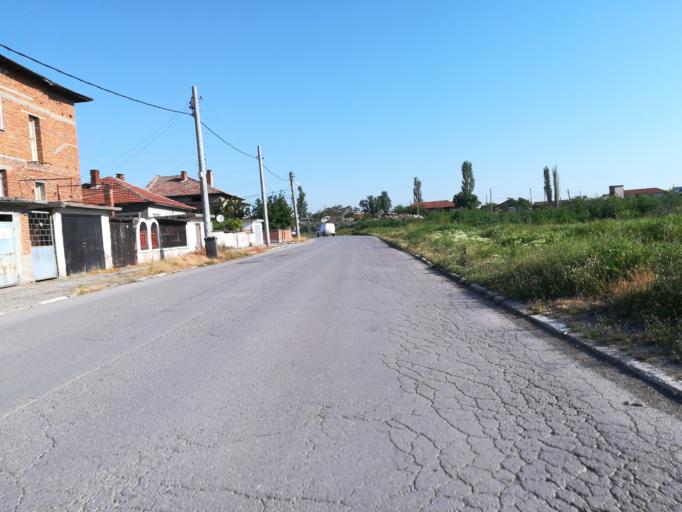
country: BG
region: Stara Zagora
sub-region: Obshtina Chirpan
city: Chirpan
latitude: 42.1065
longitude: 25.2272
